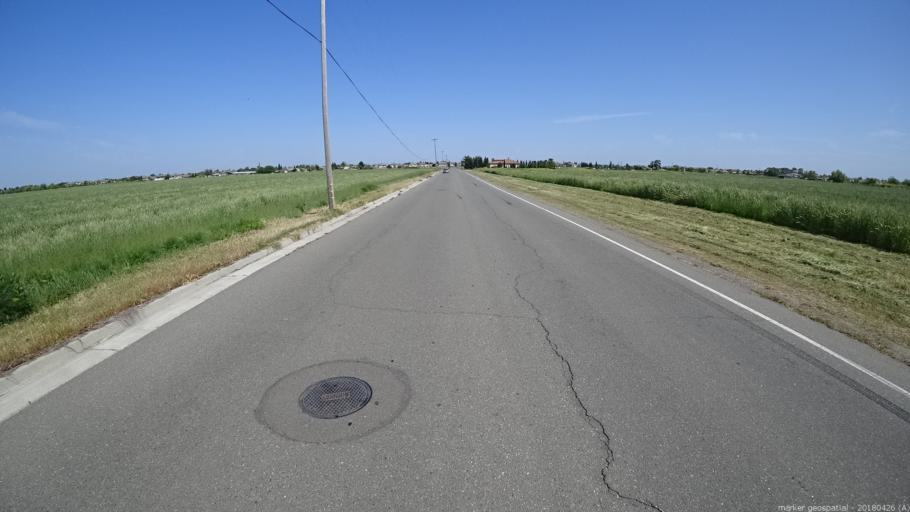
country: US
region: California
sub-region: Yolo County
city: West Sacramento
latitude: 38.5309
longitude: -121.5675
